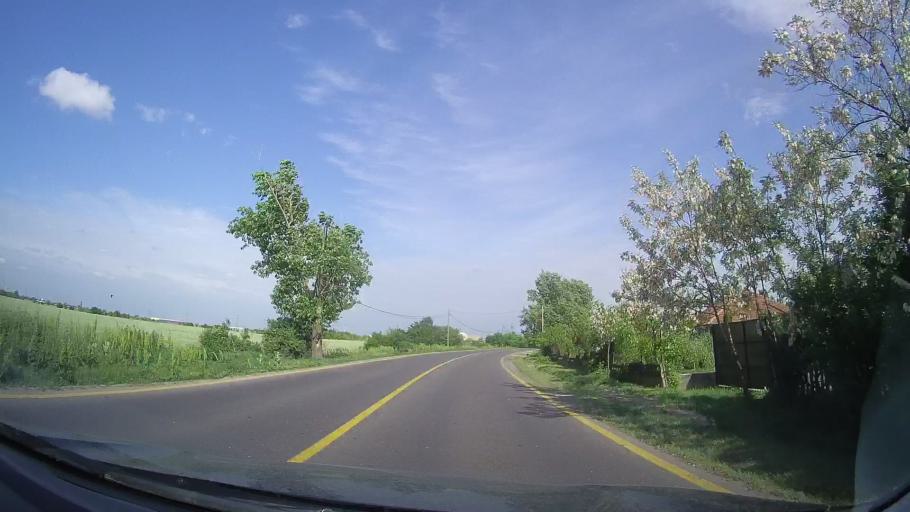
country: RO
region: Ilfov
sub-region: Comuna Magurele
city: Magurele
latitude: 44.3662
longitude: 26.0182
